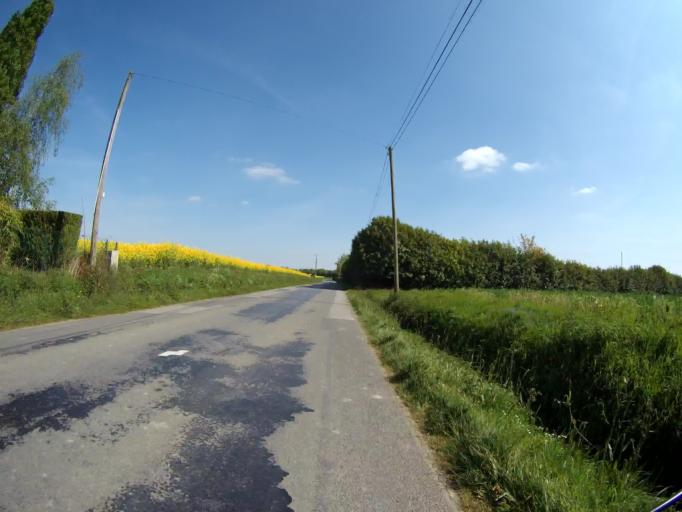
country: FR
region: Brittany
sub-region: Departement d'Ille-et-Vilaine
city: Saint-Erblon
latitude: 48.0228
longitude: -1.6364
